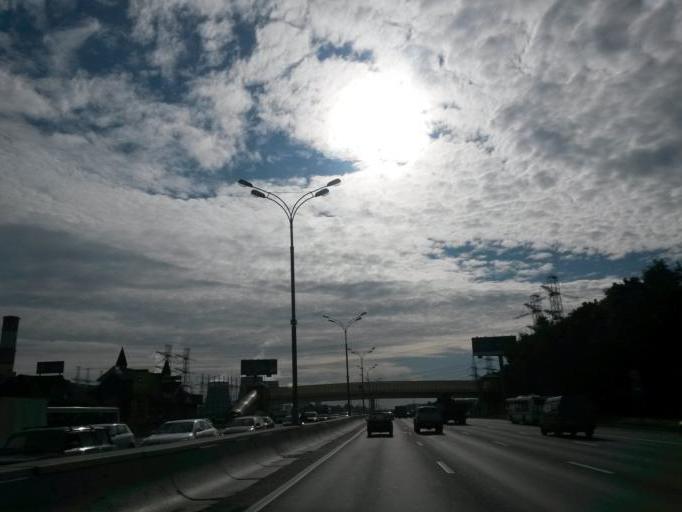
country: RU
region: Moscow
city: Annino
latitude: 55.5747
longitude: 37.6191
